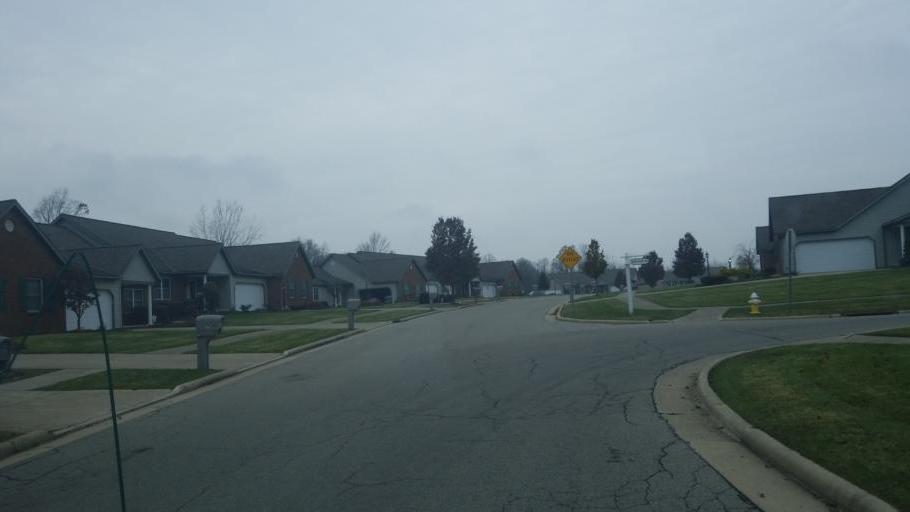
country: US
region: Ohio
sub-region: Richland County
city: Mansfield
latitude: 40.7129
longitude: -82.5279
